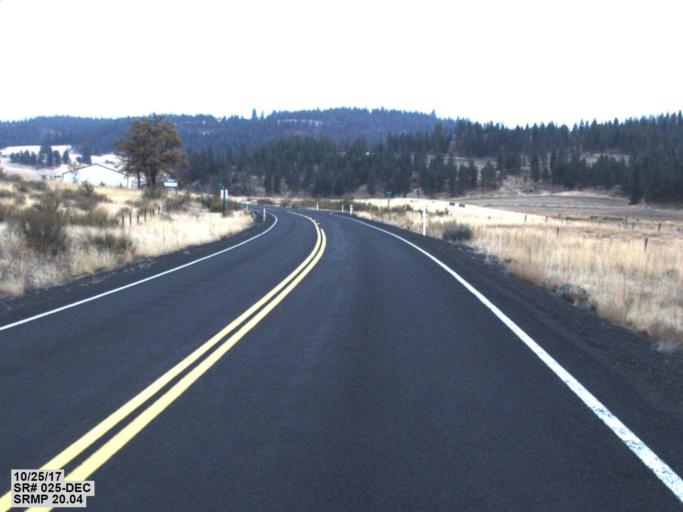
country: US
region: Washington
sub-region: Lincoln County
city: Davenport
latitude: 47.8945
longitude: -118.2729
